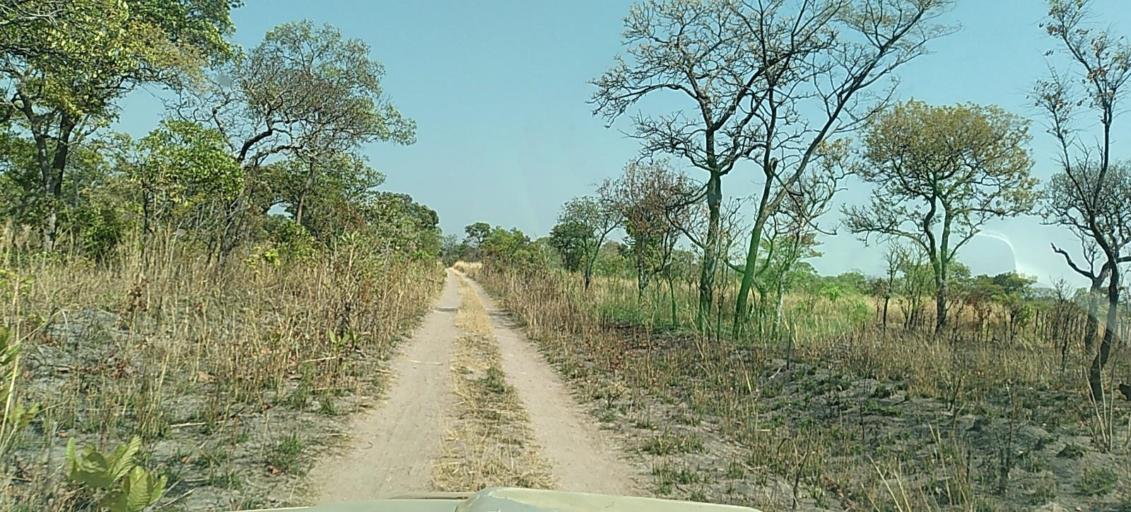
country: ZM
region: North-Western
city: Kalengwa
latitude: -13.3101
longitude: 24.8105
